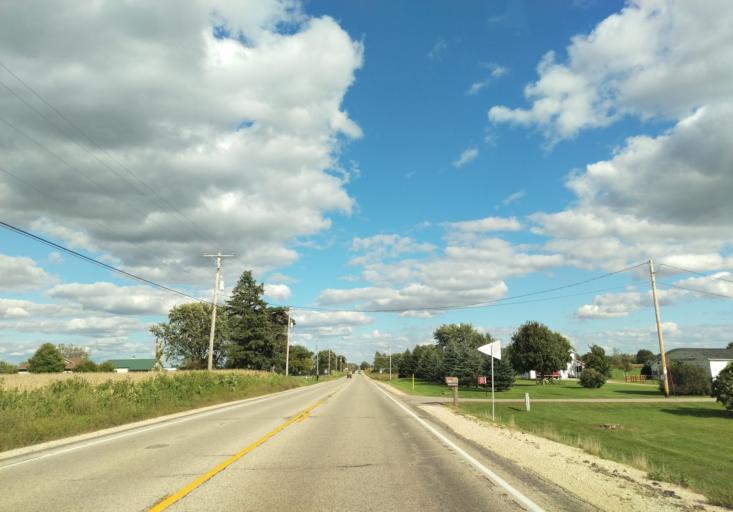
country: US
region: Wisconsin
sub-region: Rock County
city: Janesville
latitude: 42.7304
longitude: -89.1017
